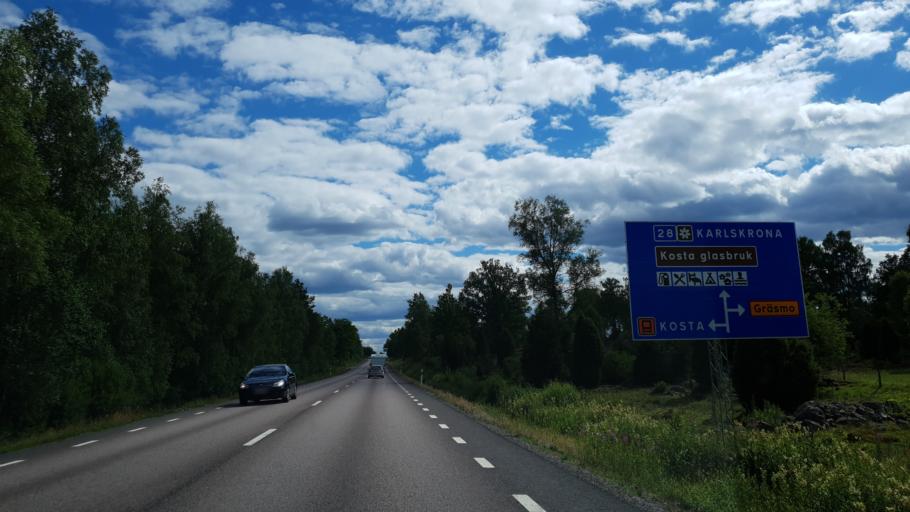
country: SE
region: Kronoberg
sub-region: Lessebo Kommun
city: Lessebo
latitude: 56.8637
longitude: 15.3873
